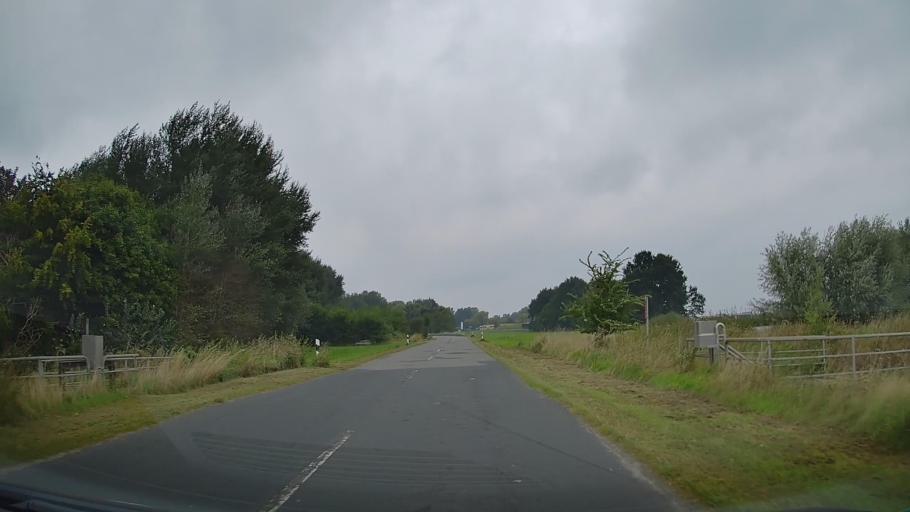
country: DE
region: Lower Saxony
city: Neuhaus an der Oste
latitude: 53.8159
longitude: 9.0409
